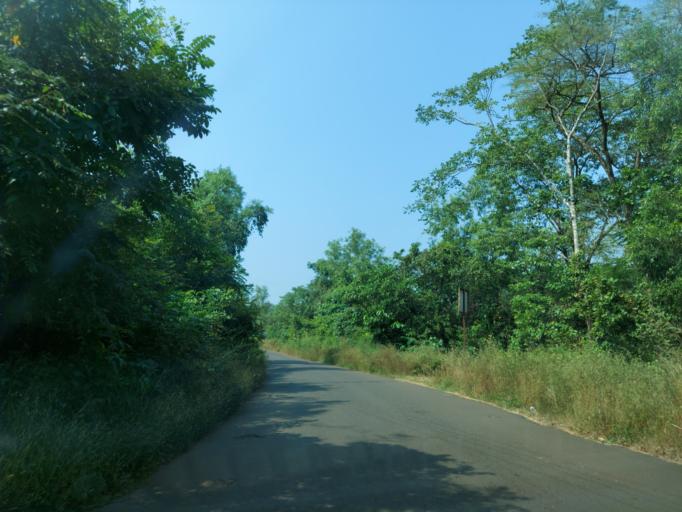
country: IN
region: Maharashtra
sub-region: Sindhudurg
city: Kudal
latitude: 15.9789
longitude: 73.6570
